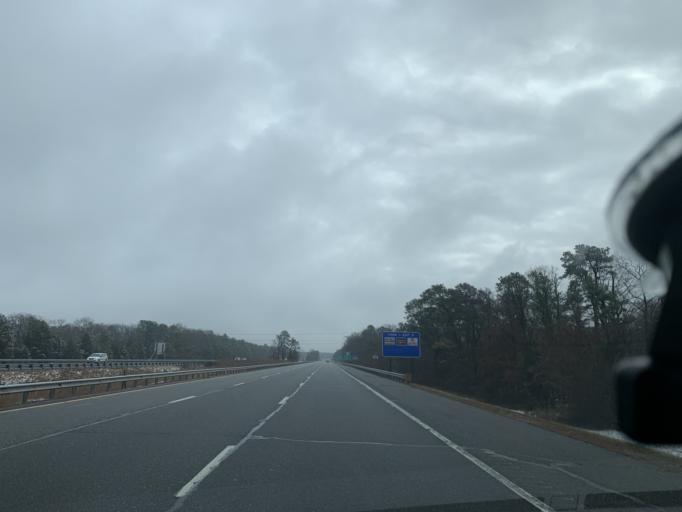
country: US
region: New Jersey
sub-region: Atlantic County
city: Pomona
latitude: 39.4413
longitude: -74.6061
